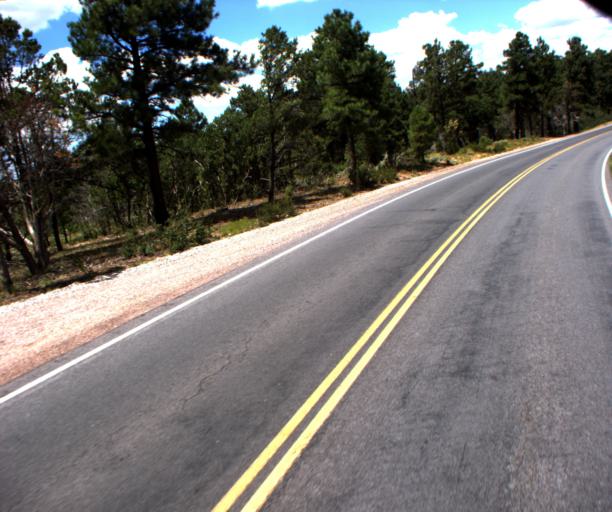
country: US
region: Arizona
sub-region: Coconino County
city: Grand Canyon
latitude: 36.0126
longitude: -112.0653
